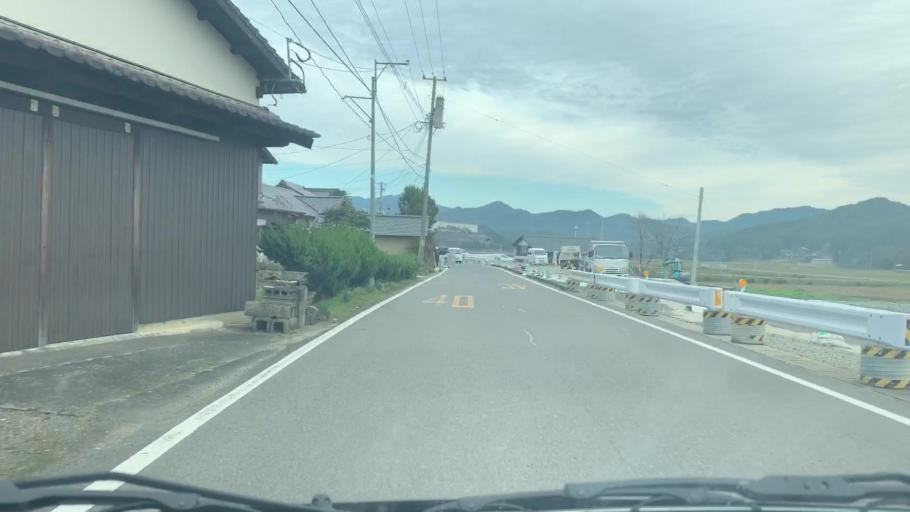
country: JP
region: Saga Prefecture
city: Takeocho-takeo
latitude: 33.2019
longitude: 129.9614
